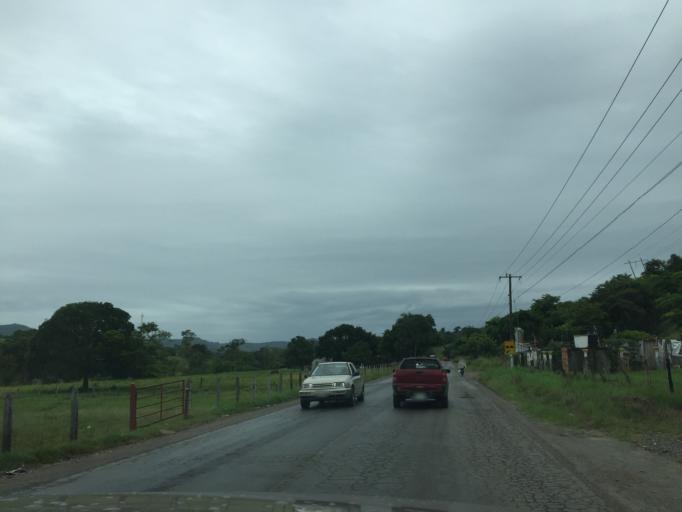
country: MX
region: Veracruz
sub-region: Papantla
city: El Chote
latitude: 20.4417
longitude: -97.4044
